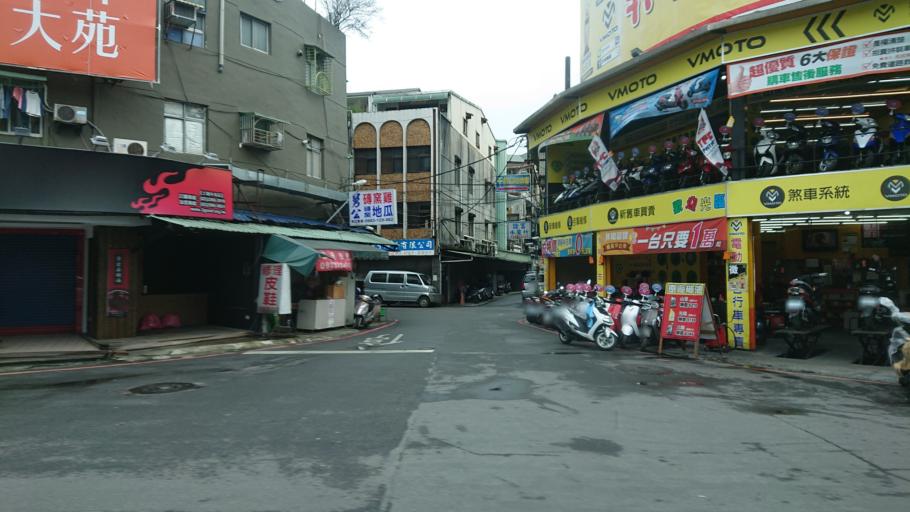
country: TW
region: Taipei
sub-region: Taipei
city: Banqiao
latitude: 24.9727
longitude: 121.4404
